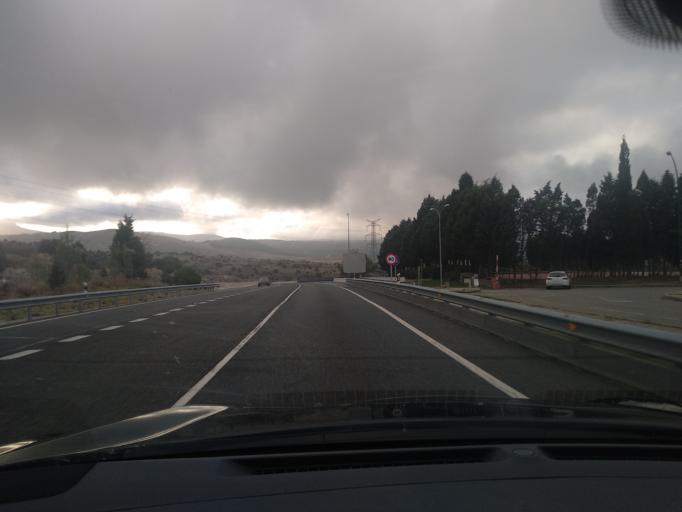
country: ES
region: Castille and Leon
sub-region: Provincia de Segovia
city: Otero de Herreros
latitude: 40.7754
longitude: -4.2074
